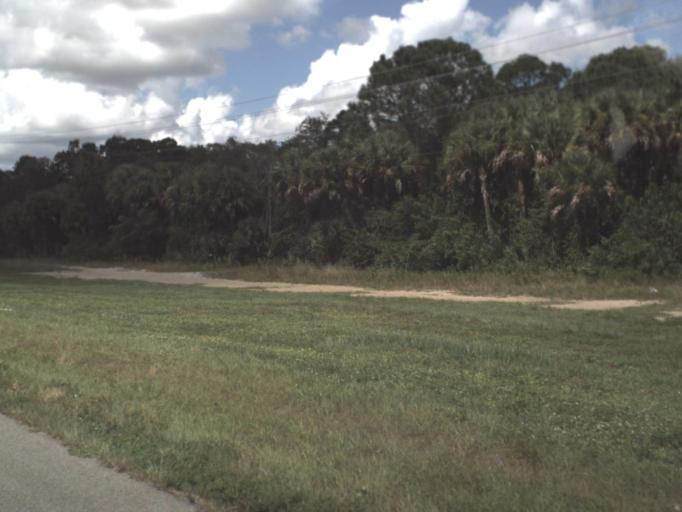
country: US
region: Florida
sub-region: Lee County
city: Lehigh Acres
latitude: 26.5545
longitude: -81.6508
